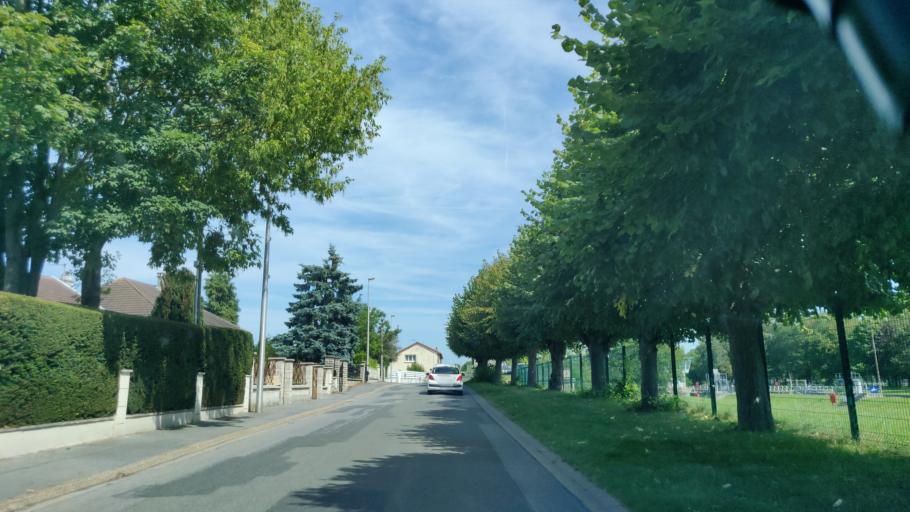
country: FR
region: Picardie
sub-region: Departement de l'Oise
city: Pont-Sainte-Maxence
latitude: 49.3060
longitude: 2.6127
